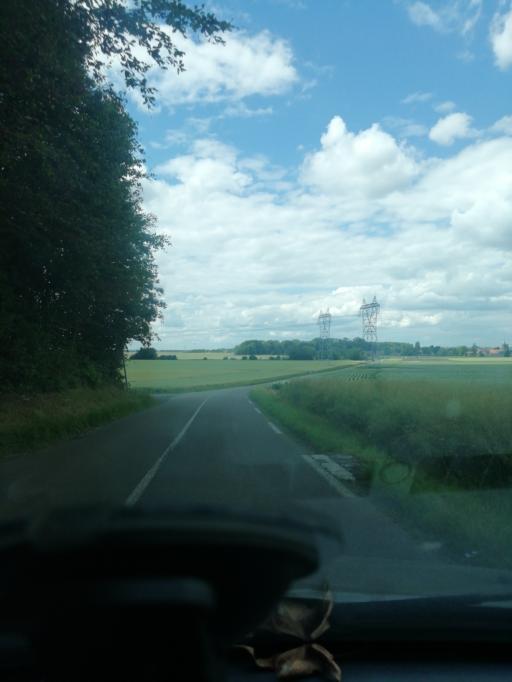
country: FR
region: Nord-Pas-de-Calais
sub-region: Departement du Nord
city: Lewarde
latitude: 50.3210
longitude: 3.1573
